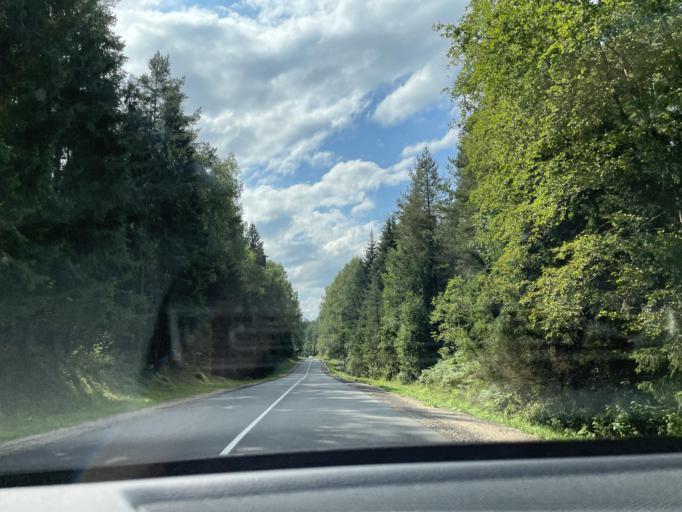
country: RU
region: Novgorod
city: Valday
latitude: 58.0302
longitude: 33.2063
